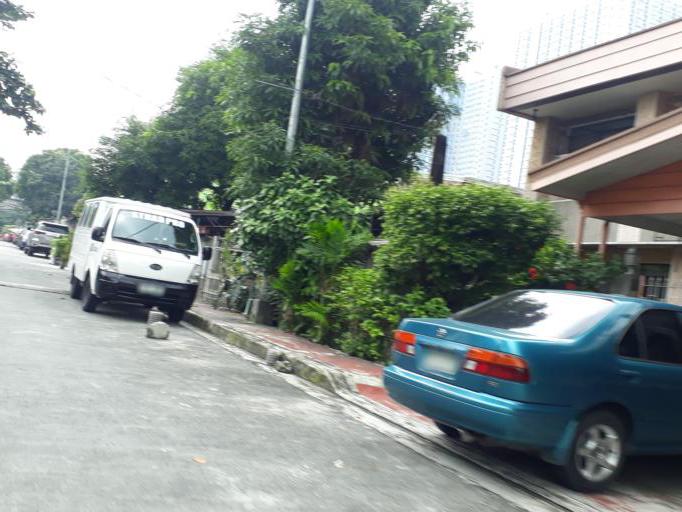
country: PH
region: Calabarzon
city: Bagong Pagasa
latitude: 14.6615
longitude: 121.0313
